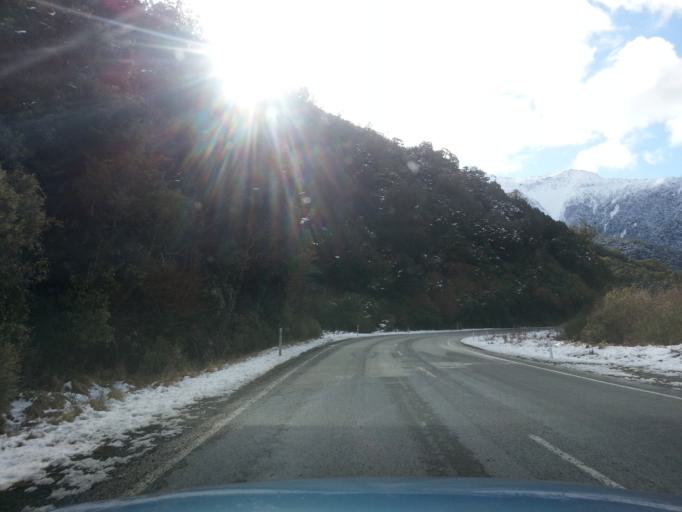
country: NZ
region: West Coast
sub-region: Grey District
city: Greymouth
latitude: -42.8216
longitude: 171.5632
